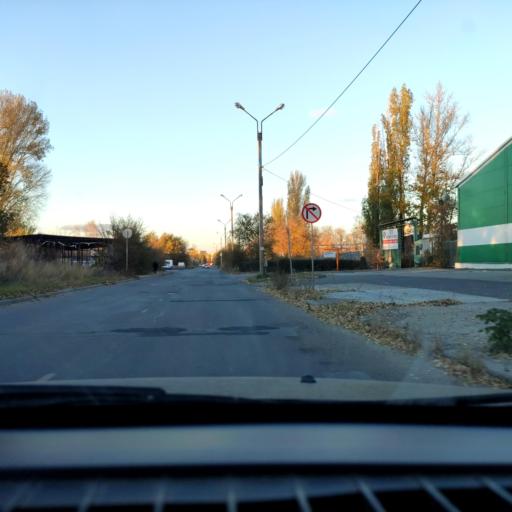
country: RU
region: Samara
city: Tol'yatti
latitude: 53.5532
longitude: 49.3137
